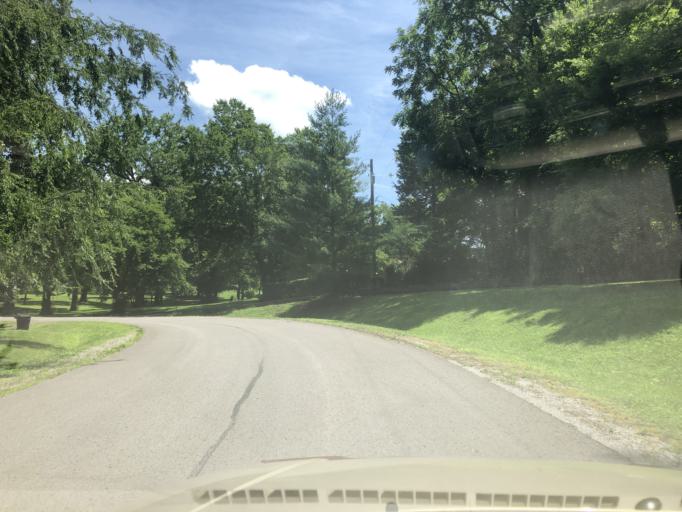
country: US
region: Tennessee
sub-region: Davidson County
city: Lakewood
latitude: 36.2466
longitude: -86.6834
